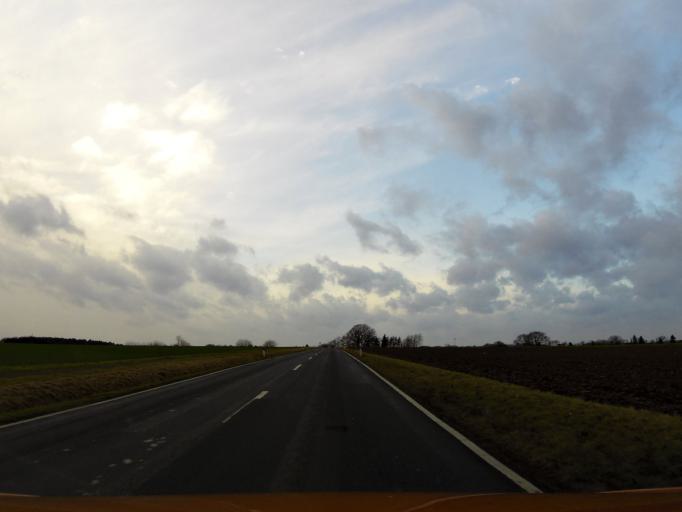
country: DE
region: Lower Saxony
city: Gross Twulpstedt
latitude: 52.3872
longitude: 10.8618
